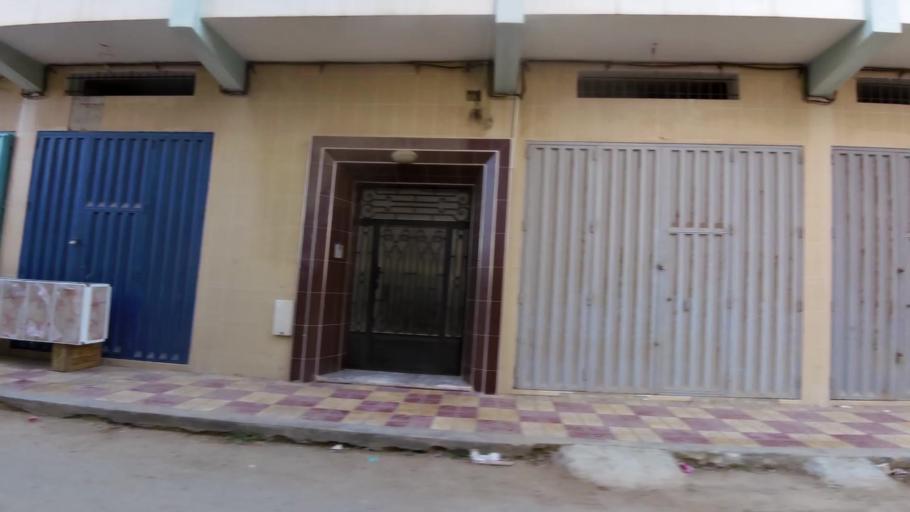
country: MA
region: Tanger-Tetouan
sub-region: Tetouan
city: Martil
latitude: 35.6100
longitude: -5.2888
